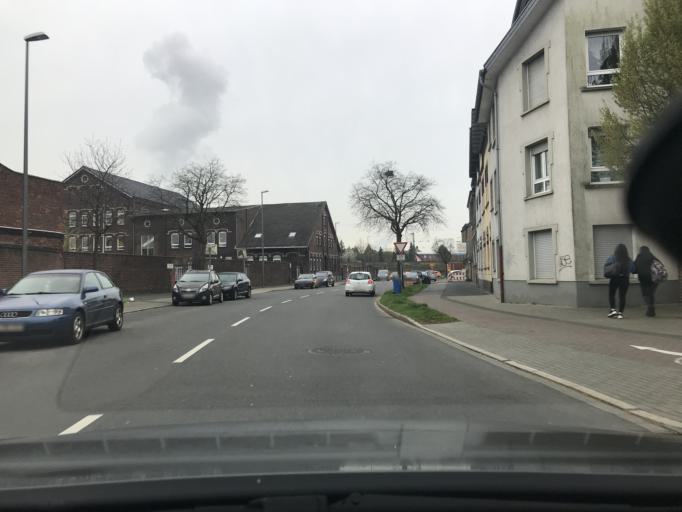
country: DE
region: North Rhine-Westphalia
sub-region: Regierungsbezirk Dusseldorf
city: Krefeld
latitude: 51.3569
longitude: 6.6425
